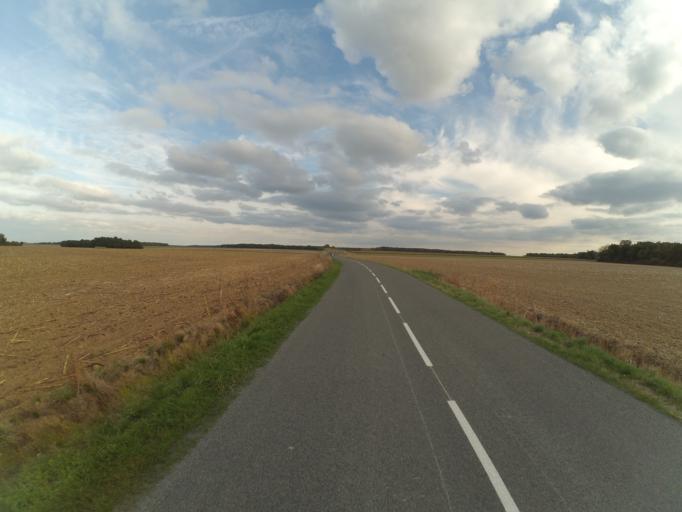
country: FR
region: Centre
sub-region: Departement d'Indre-et-Loire
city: Reugny
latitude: 47.4723
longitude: 0.9081
